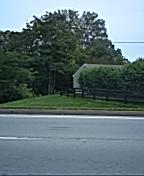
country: US
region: Kentucky
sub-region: Jefferson County
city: Hurstbourne
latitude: 38.2327
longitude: -85.5770
